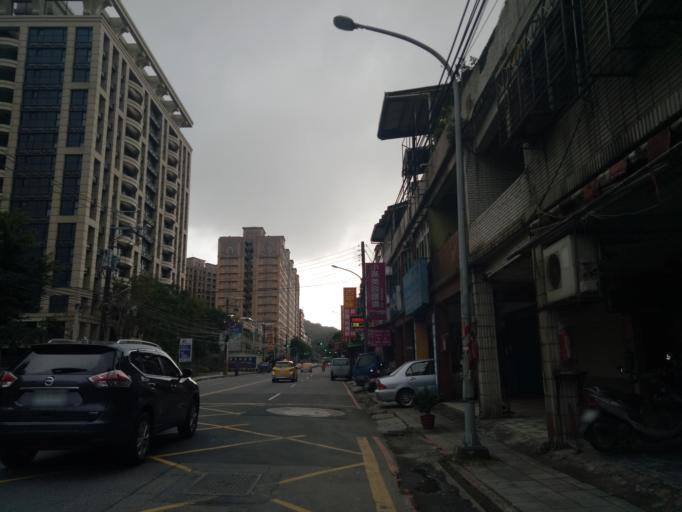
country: TW
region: Taipei
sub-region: Taipei
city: Banqiao
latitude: 24.9554
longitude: 121.4134
